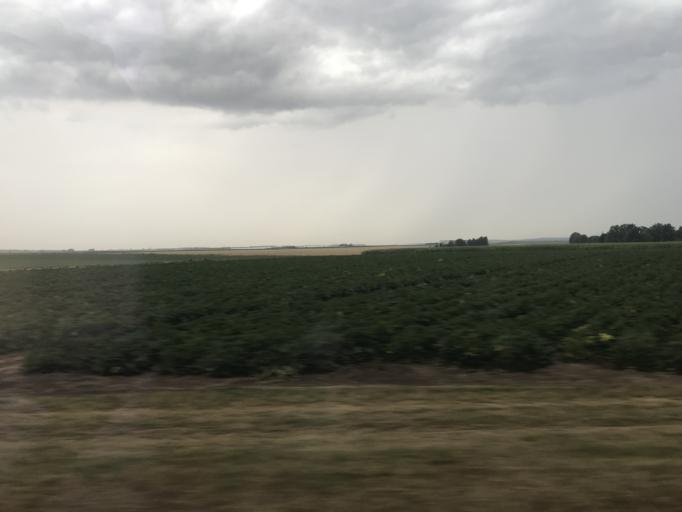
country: DE
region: Bavaria
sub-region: Regierungsbezirk Unterfranken
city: Bergtheim
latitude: 49.8937
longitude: 10.0794
